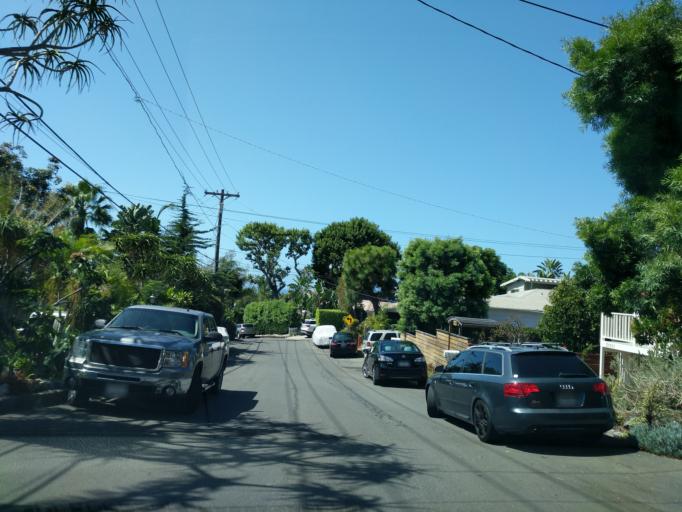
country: US
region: California
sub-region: Orange County
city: Laguna Niguel
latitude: 33.5052
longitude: -117.7416
